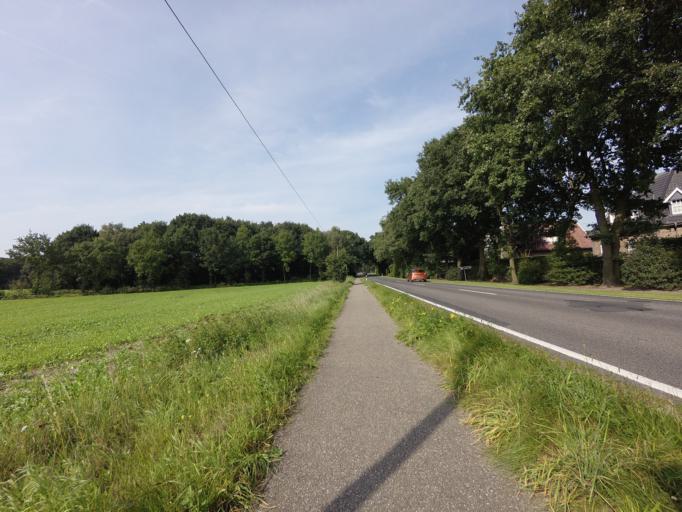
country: DE
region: Lower Saxony
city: Getelo
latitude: 52.4656
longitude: 6.8397
